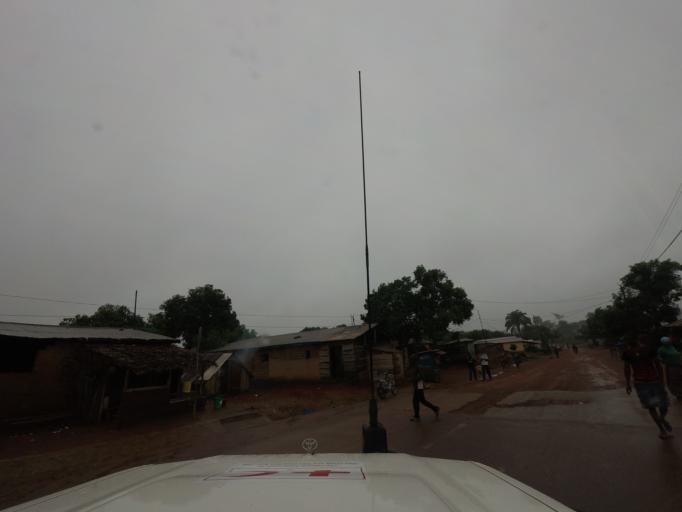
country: GN
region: Nzerekore
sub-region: Nzerekore Prefecture
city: Nzerekore
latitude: 7.7322
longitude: -8.8358
